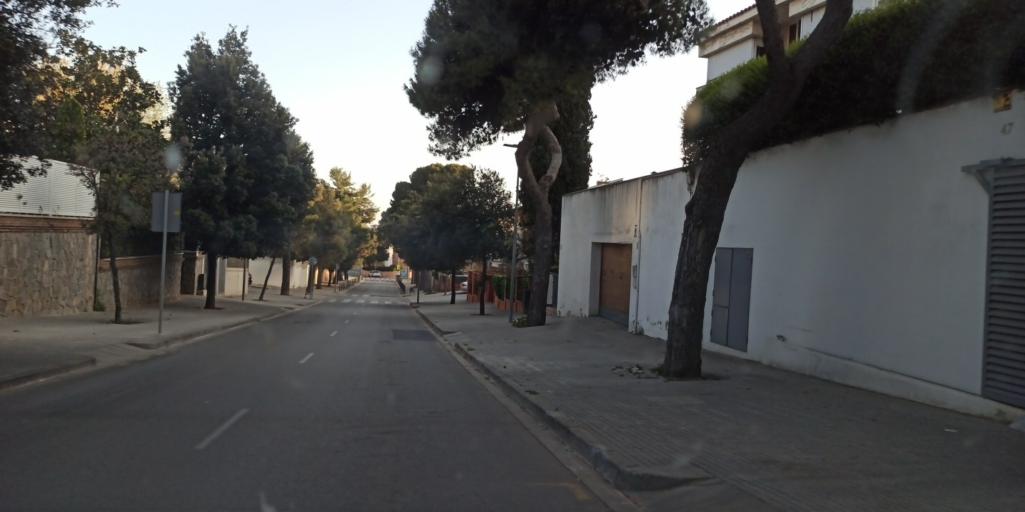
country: ES
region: Catalonia
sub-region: Provincia de Barcelona
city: Esplugues de Llobregat
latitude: 41.3860
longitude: 2.0851
